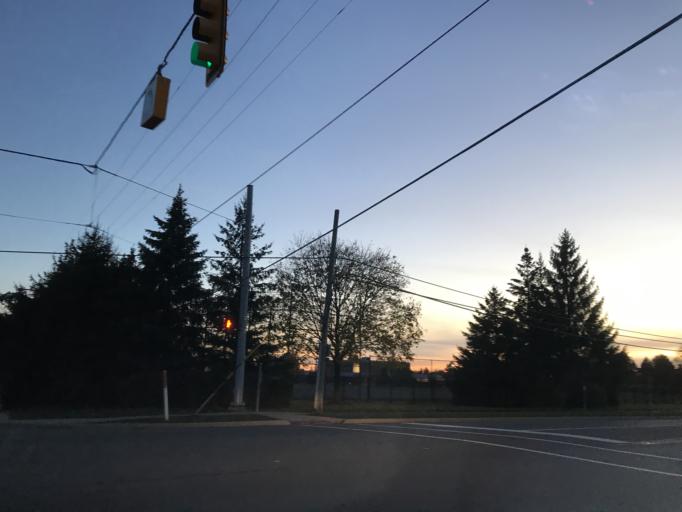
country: US
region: Michigan
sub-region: Oakland County
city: Farmington
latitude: 42.4701
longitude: -83.3671
